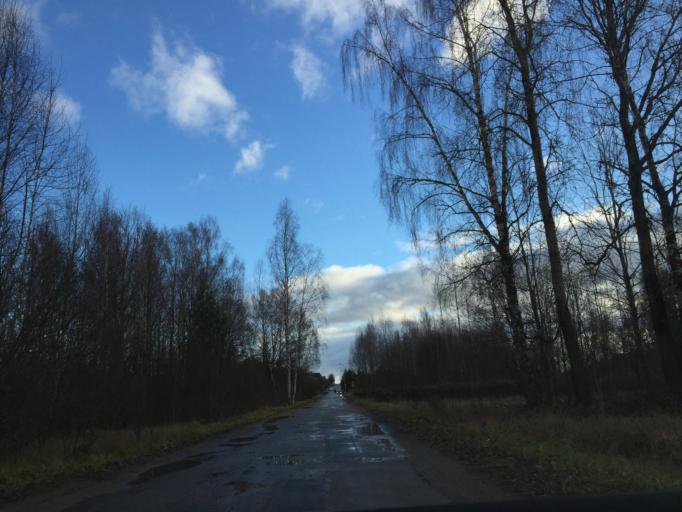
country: LV
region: Koceni
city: Koceni
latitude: 57.5365
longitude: 25.3802
